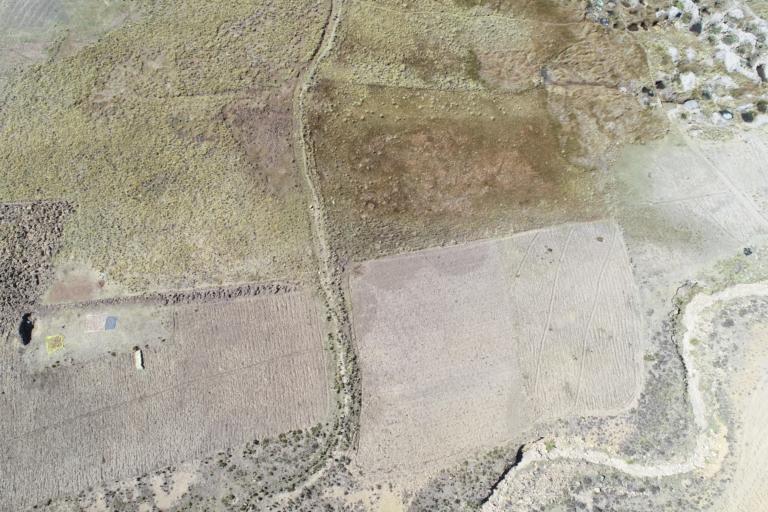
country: BO
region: La Paz
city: Achacachi
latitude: -15.8852
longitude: -68.8096
